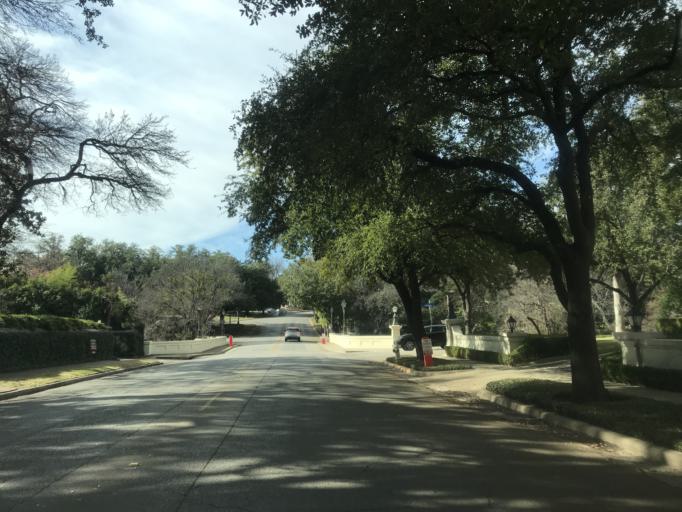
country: US
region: Texas
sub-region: Dallas County
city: Highland Park
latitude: 32.8233
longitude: -96.8000
